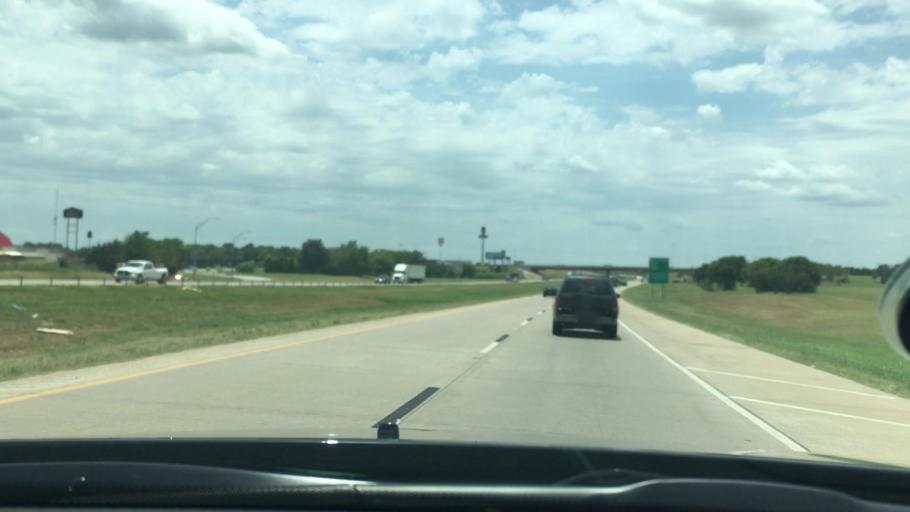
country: US
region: Oklahoma
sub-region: Carter County
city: Ardmore
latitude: 34.1922
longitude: -97.1650
